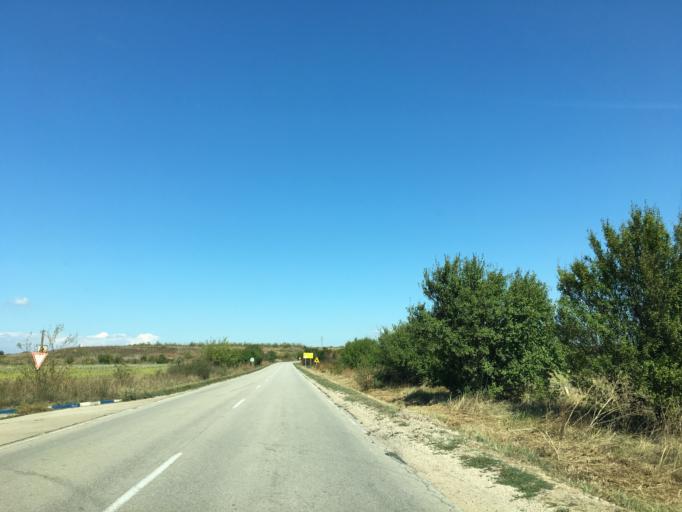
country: BG
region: Montana
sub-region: Obshtina Brusartsi
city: Brusartsi
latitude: 43.7054
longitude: 23.0091
